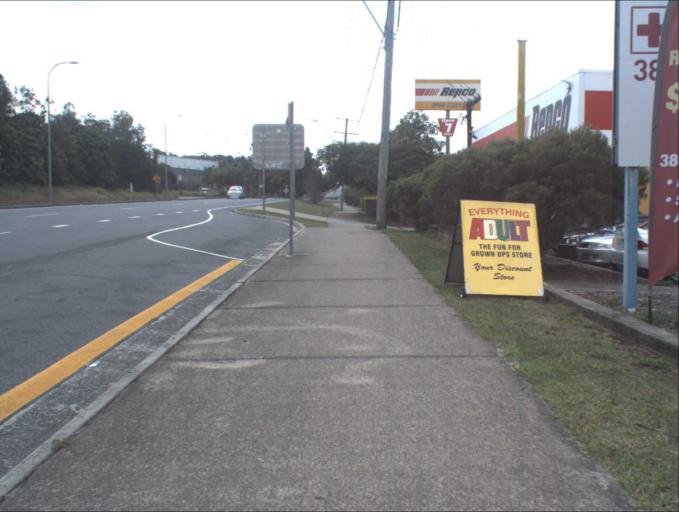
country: AU
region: Queensland
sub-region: Brisbane
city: Sunnybank Hills
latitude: -27.6592
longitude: 153.0386
